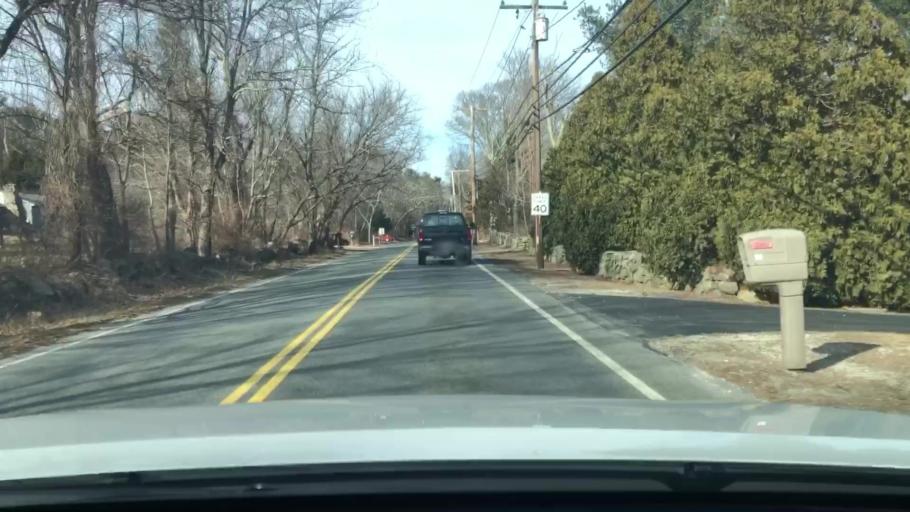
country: US
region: Massachusetts
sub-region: Worcester County
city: Mendon
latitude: 42.0894
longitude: -71.5333
